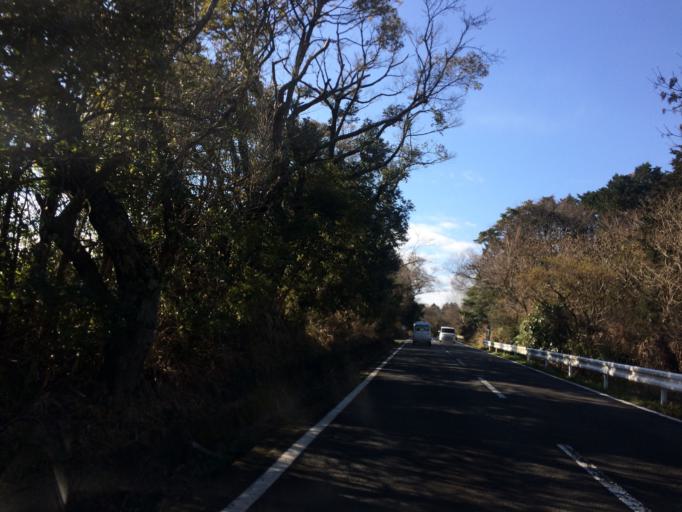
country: JP
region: Shizuoka
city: Shizuoka-shi
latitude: 34.9696
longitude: 138.4481
